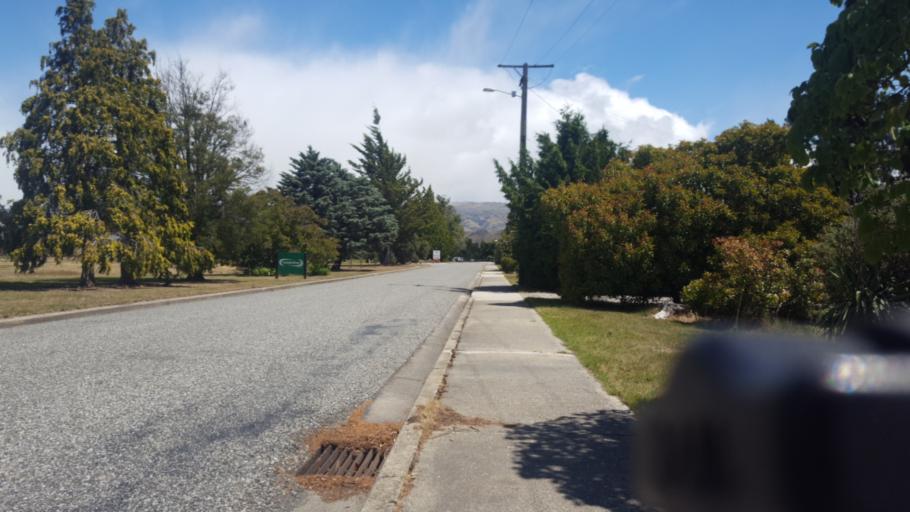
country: NZ
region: Otago
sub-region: Queenstown-Lakes District
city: Wanaka
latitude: -45.1992
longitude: 169.3318
